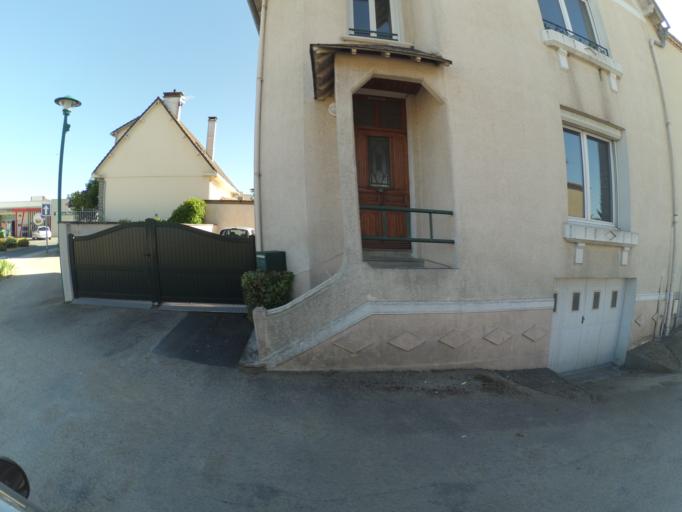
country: FR
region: Pays de la Loire
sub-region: Departement de la Vendee
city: Beaurepaire
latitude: 46.9079
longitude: -1.1348
